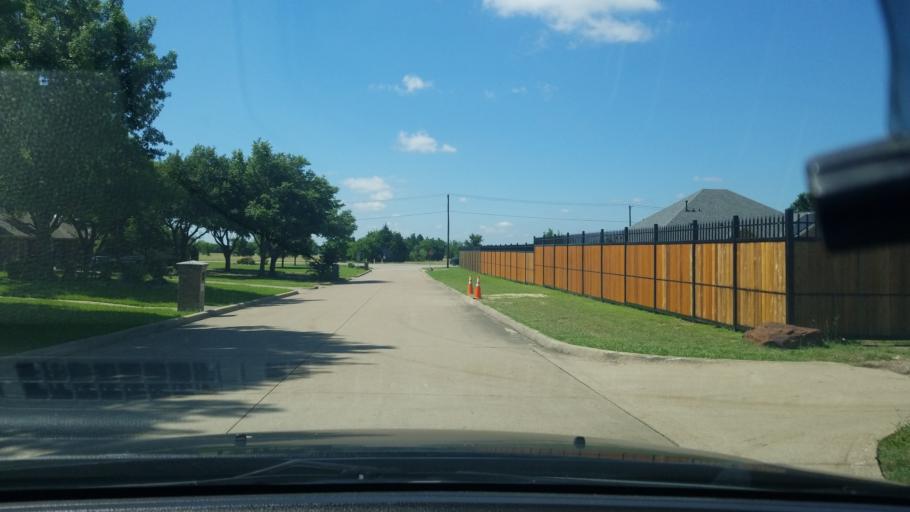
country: US
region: Texas
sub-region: Dallas County
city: Sunnyvale
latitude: 32.7974
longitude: -96.5891
